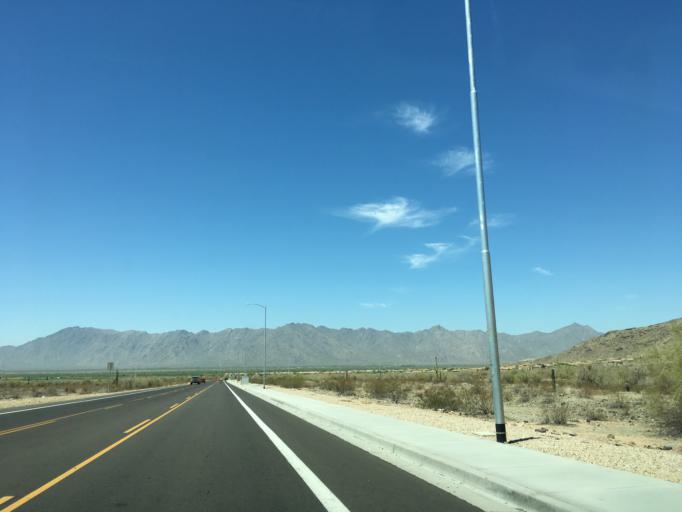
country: US
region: Arizona
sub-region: Maricopa County
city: Laveen
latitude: 33.3020
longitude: -112.1051
